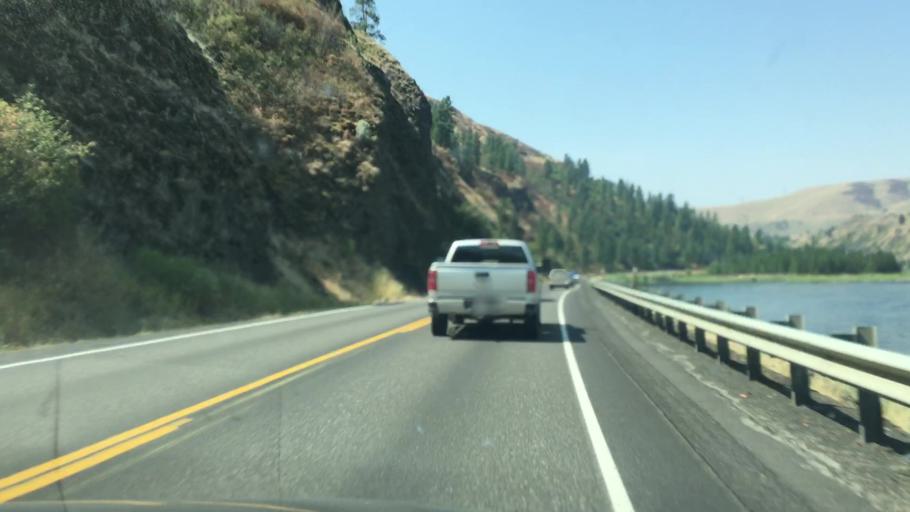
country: US
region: Idaho
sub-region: Nez Perce County
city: Lapwai
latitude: 46.4904
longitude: -116.7291
